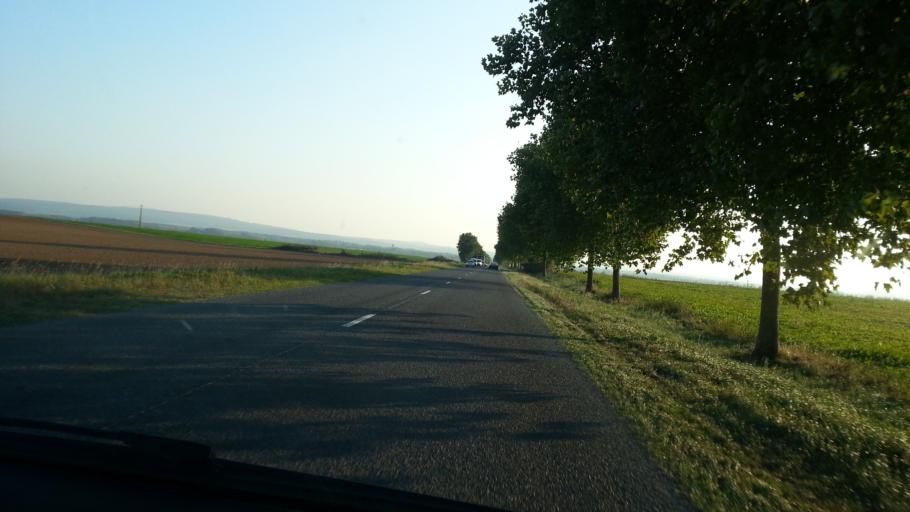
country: FR
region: Picardie
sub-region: Departement de l'Oise
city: Saint-Martin-Longueau
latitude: 49.3711
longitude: 2.6159
